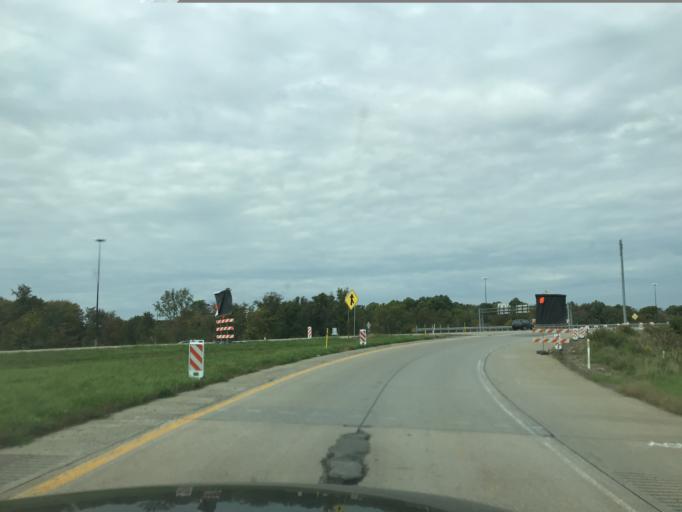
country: US
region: Pennsylvania
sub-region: Erie County
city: Erie
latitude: 42.0299
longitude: -80.1216
